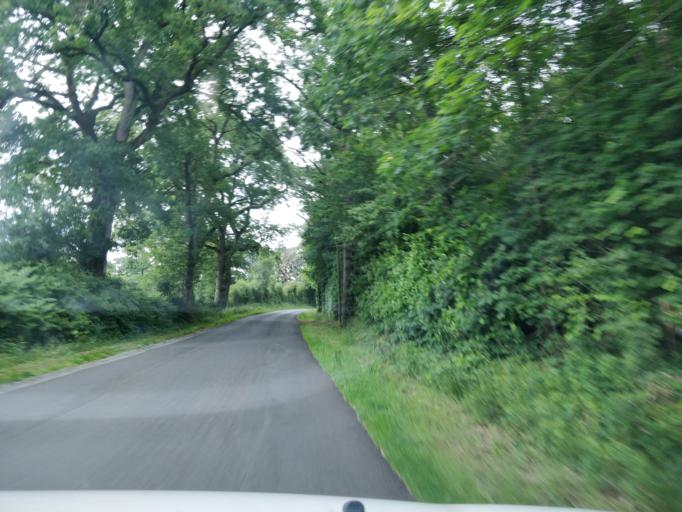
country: FR
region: Pays de la Loire
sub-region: Departement de Maine-et-Loire
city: Feneu
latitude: 47.5964
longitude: -0.6094
